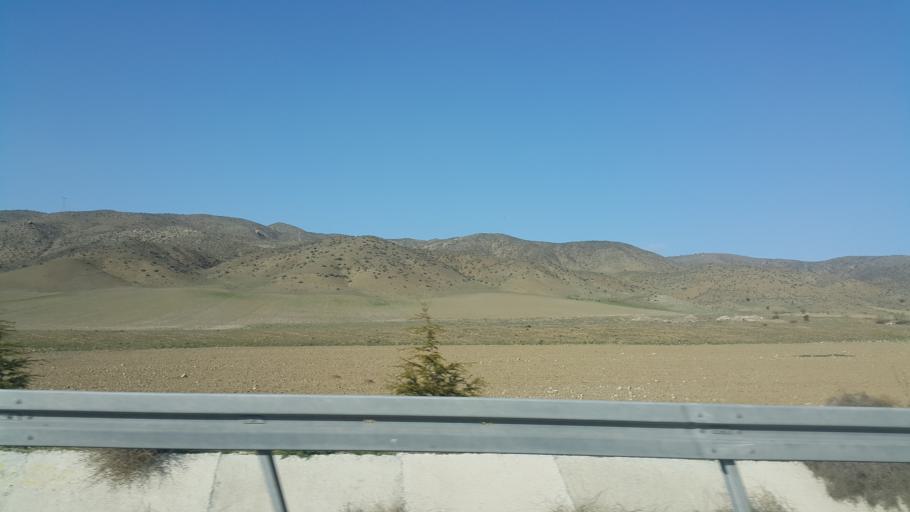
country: TR
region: Ankara
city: Sereflikochisar
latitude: 38.8077
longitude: 33.6115
